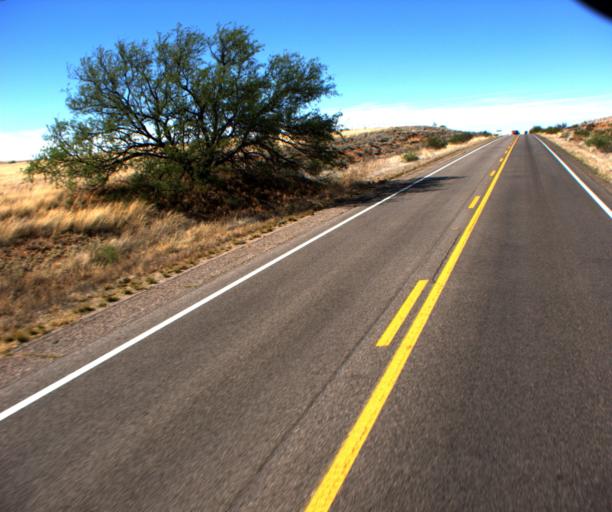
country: US
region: Arizona
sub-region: Pima County
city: Corona de Tucson
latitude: 31.7094
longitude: -110.6555
